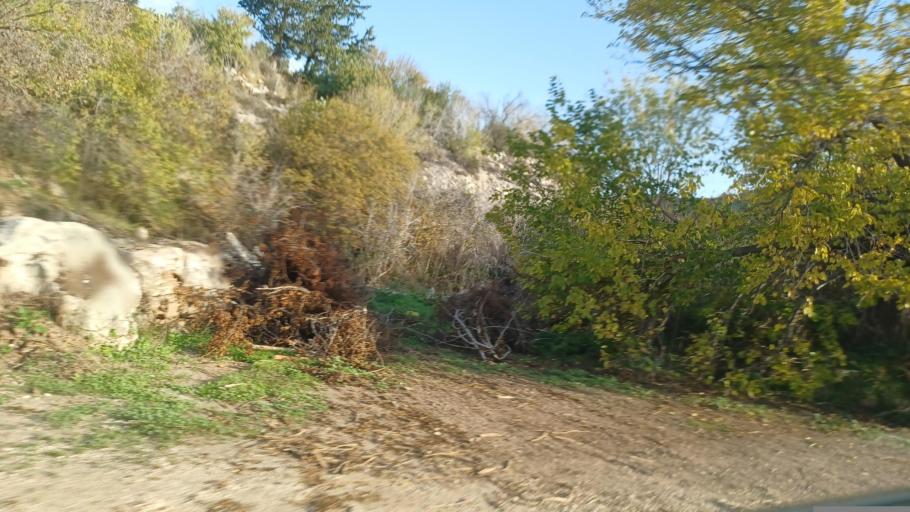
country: CY
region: Pafos
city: Mesogi
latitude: 34.7905
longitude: 32.4943
